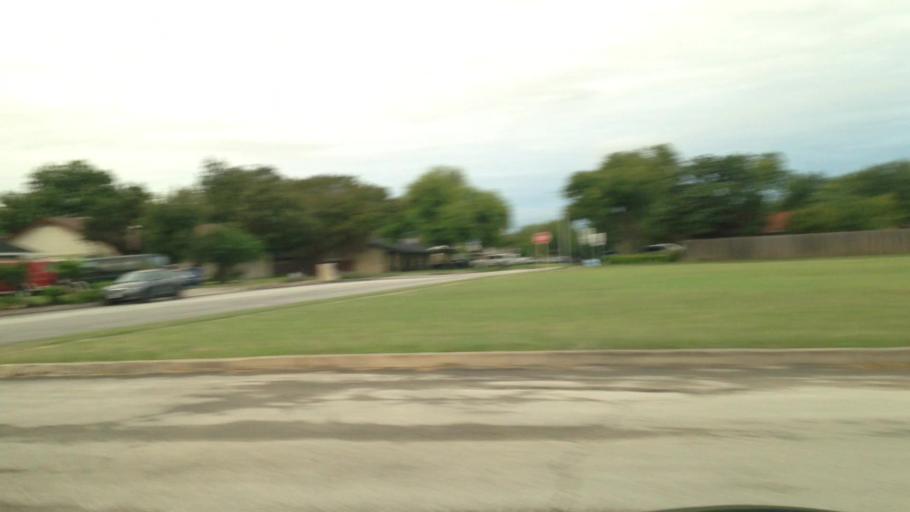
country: US
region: Texas
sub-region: Bexar County
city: Windcrest
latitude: 29.5047
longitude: -98.3819
